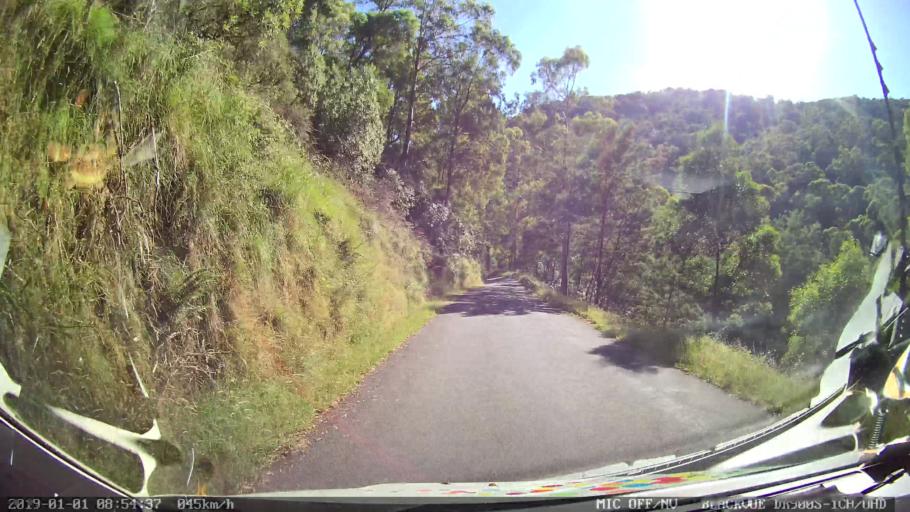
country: AU
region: New South Wales
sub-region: Snowy River
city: Jindabyne
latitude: -36.2590
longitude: 148.1925
